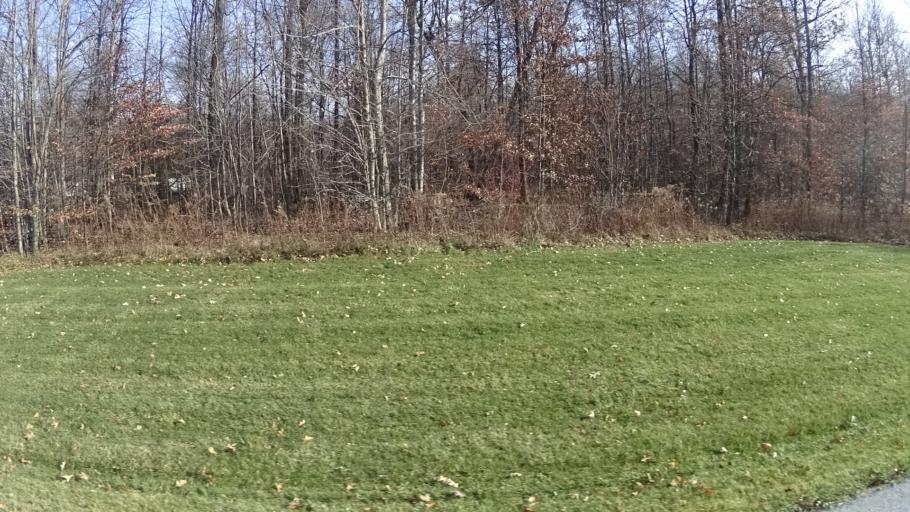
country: US
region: Ohio
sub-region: Lorain County
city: Grafton
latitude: 41.2181
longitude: -82.0349
